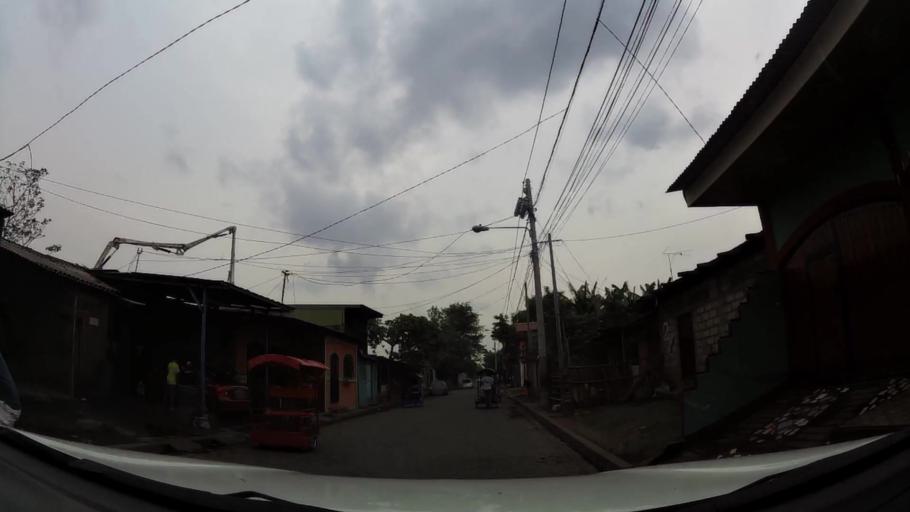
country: NI
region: Leon
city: Leon
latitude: 12.4454
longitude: -86.8713
